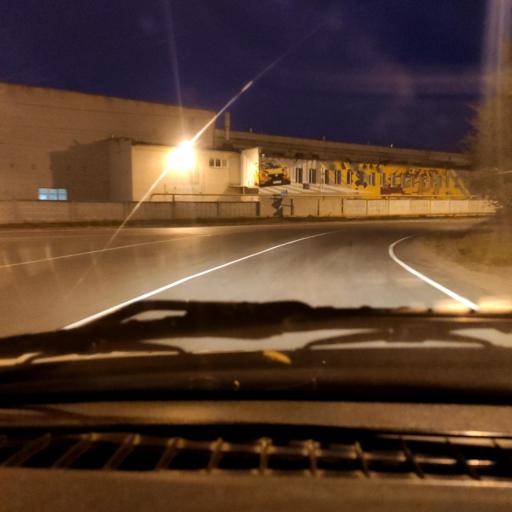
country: RU
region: Samara
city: Zhigulevsk
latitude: 53.4644
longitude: 49.5482
